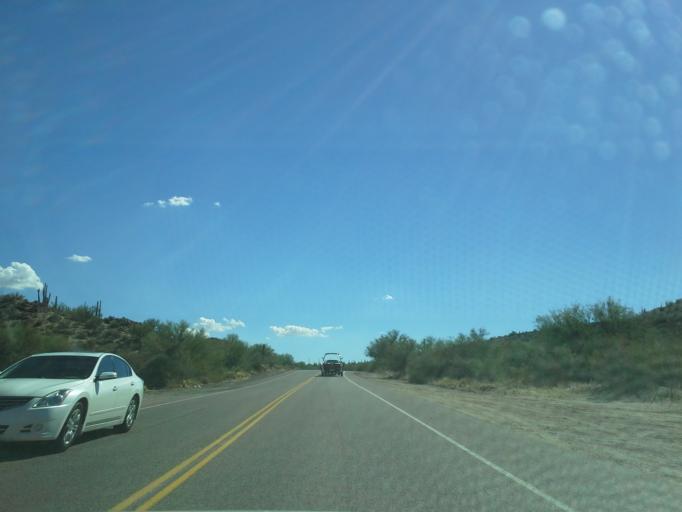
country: US
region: Arizona
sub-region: Pinal County
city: Apache Junction
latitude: 33.5051
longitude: -111.6179
